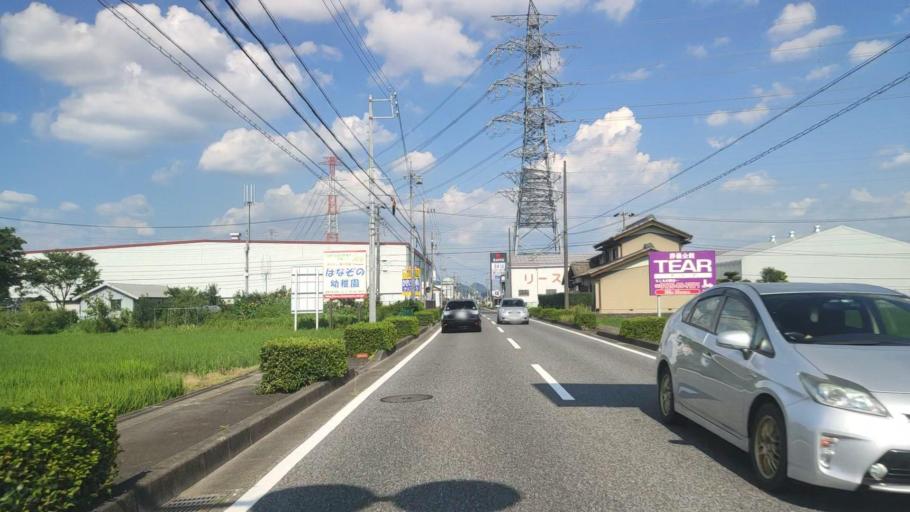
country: JP
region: Gifu
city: Gifu-shi
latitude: 35.4504
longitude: 136.7079
